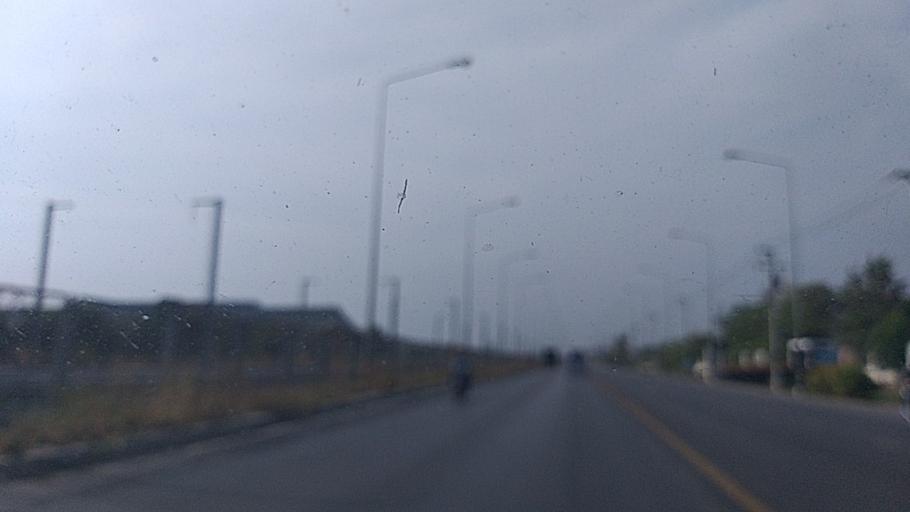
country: TH
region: Bangkok
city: Don Mueang
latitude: 13.9590
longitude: 100.6059
